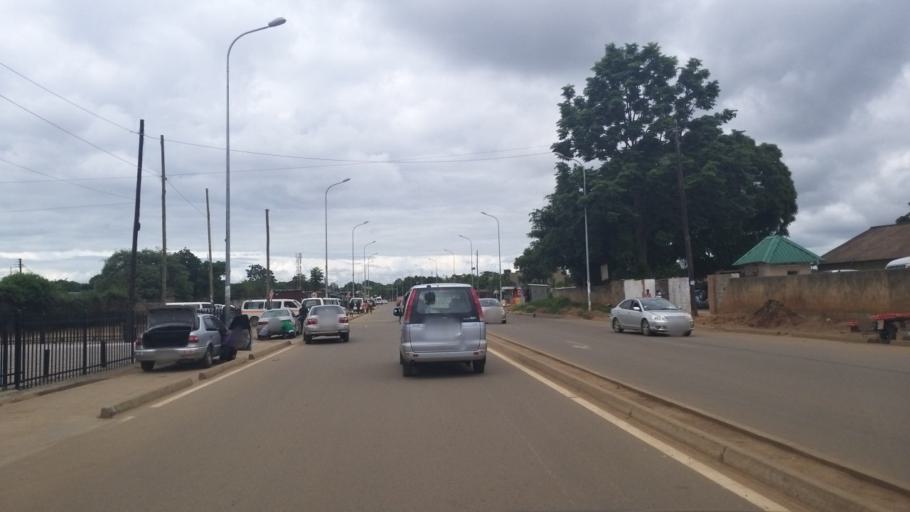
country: ZM
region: Lusaka
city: Lusaka
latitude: -15.4401
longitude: 28.3106
